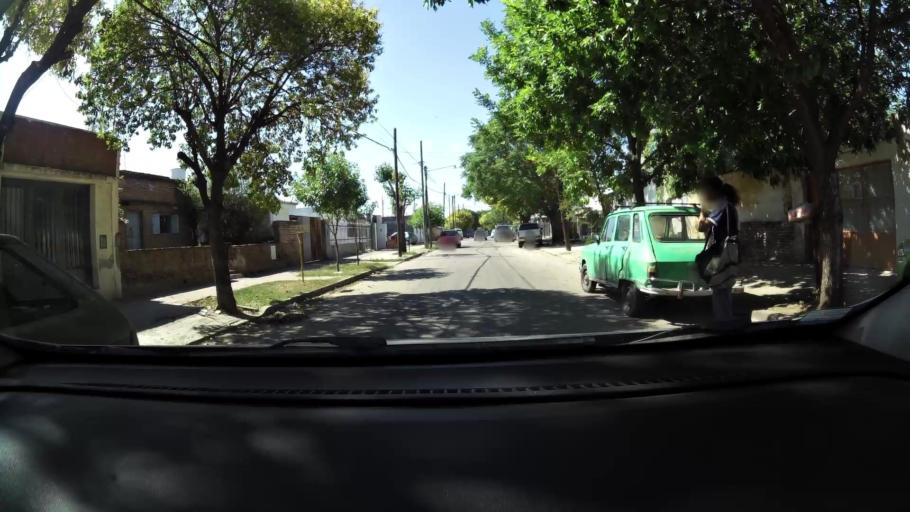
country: AR
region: Cordoba
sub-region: Departamento de Capital
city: Cordoba
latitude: -31.3700
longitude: -64.1748
